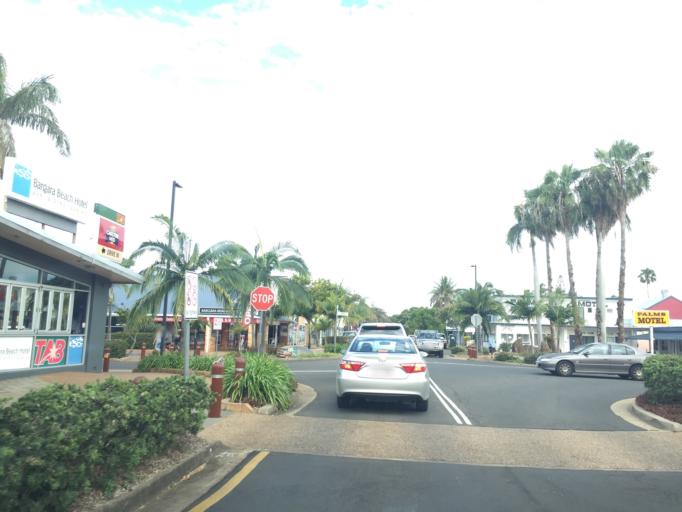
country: AU
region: Queensland
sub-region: Bundaberg
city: Bundaberg
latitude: -24.8147
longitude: 152.4628
